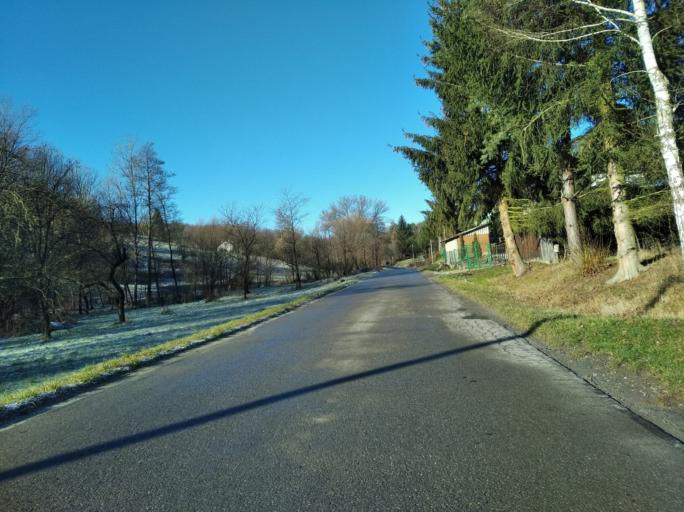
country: PL
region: Subcarpathian Voivodeship
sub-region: Powiat strzyzowski
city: Czudec
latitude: 49.9504
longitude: 21.7776
